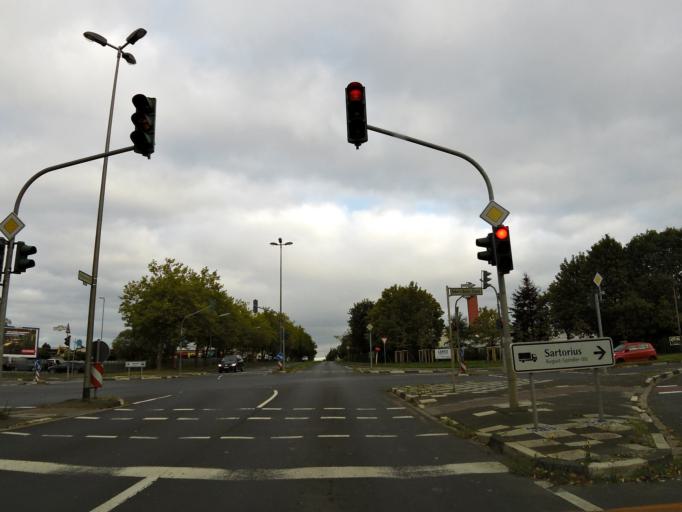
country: DE
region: Lower Saxony
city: Goettingen
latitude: 51.5480
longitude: 9.8898
